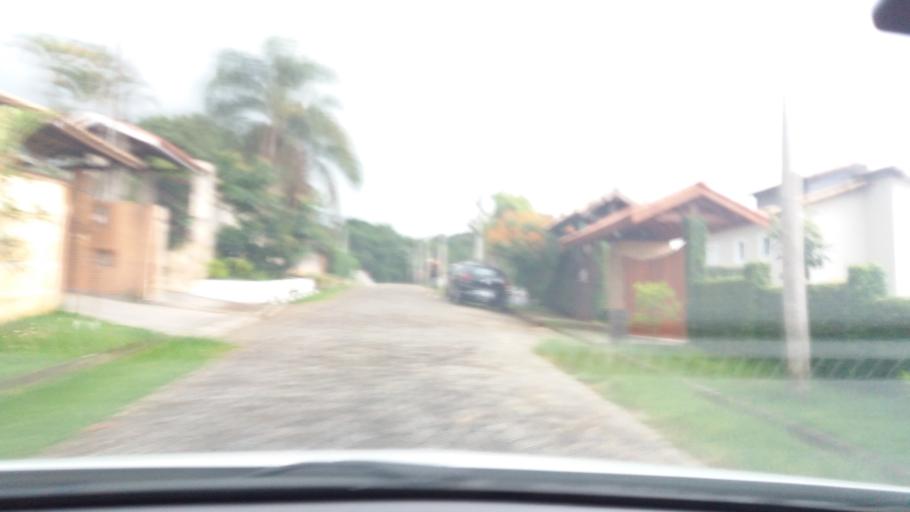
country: BR
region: Sao Paulo
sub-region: Bom Jesus Dos Perdoes
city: Bom Jesus dos Perdoes
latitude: -23.1715
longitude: -46.4566
